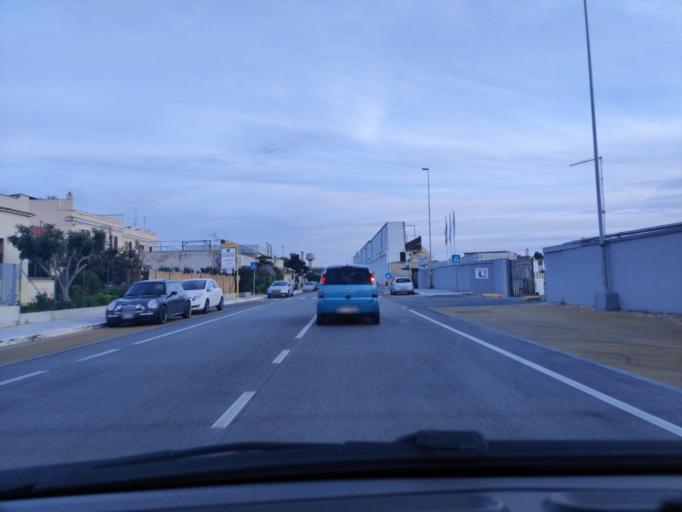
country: IT
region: Latium
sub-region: Citta metropolitana di Roma Capitale
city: Civitavecchia
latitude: 42.1068
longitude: 11.7820
